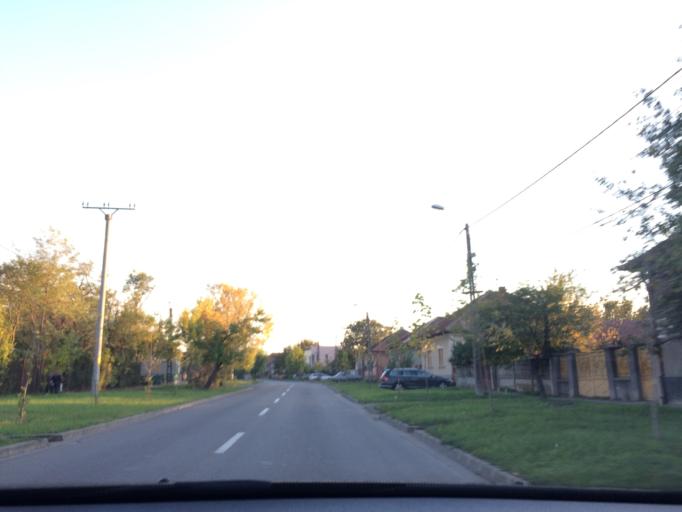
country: RO
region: Timis
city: Timisoara
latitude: 45.7647
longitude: 21.1950
